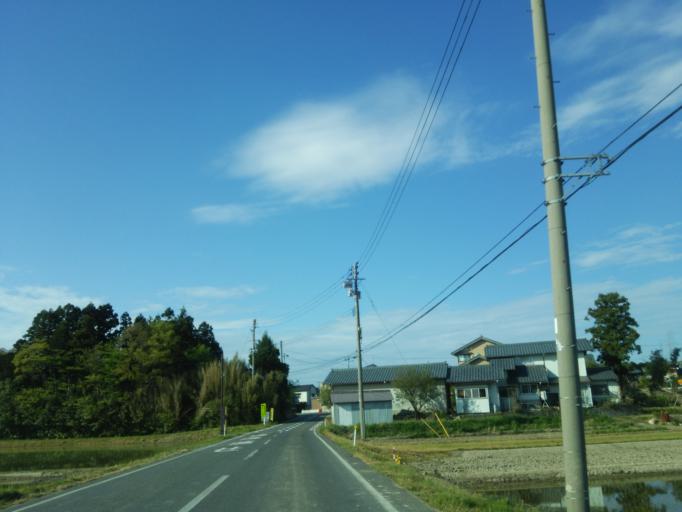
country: JP
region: Niigata
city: Niitsu-honcho
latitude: 37.8340
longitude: 139.1707
